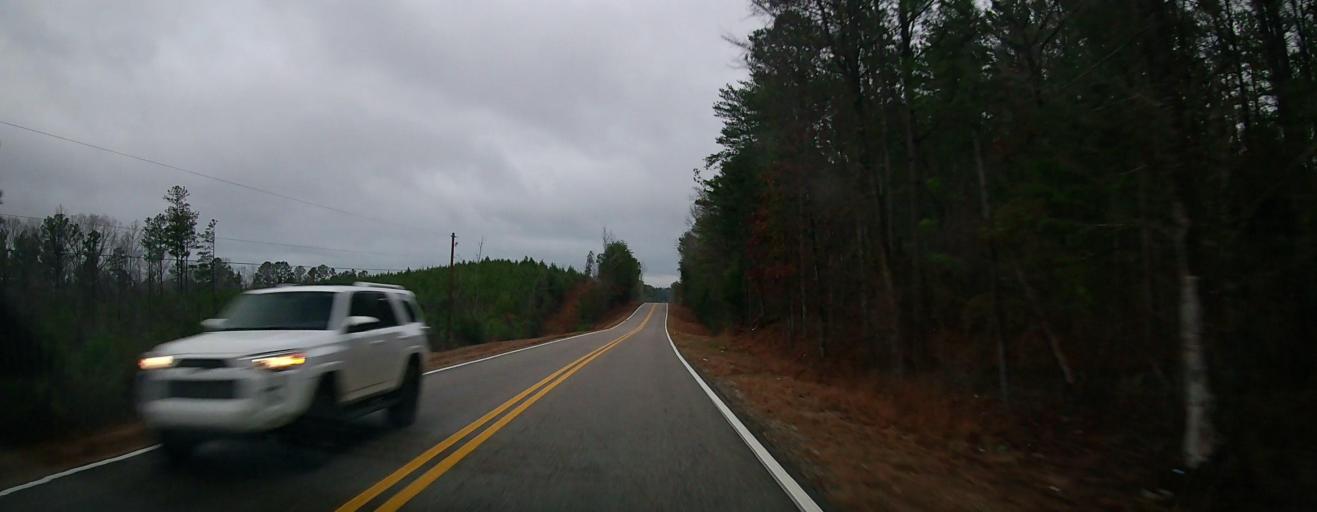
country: US
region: Alabama
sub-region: Bibb County
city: Centreville
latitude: 33.0156
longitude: -87.1465
